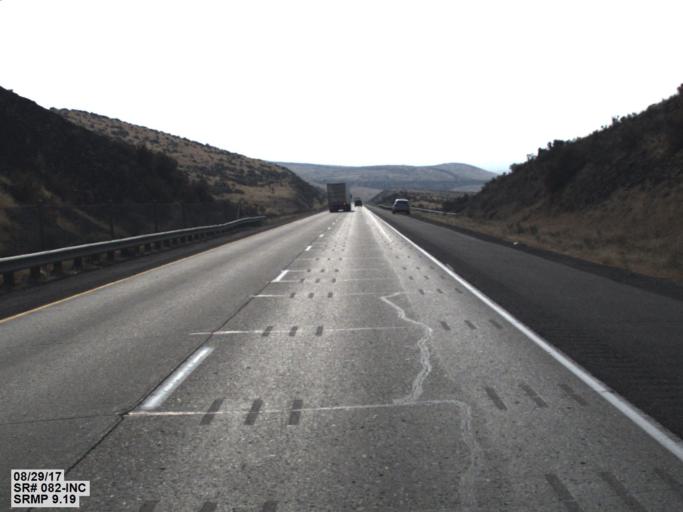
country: US
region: Washington
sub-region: Kittitas County
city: Kittitas
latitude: 46.8677
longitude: -120.4125
